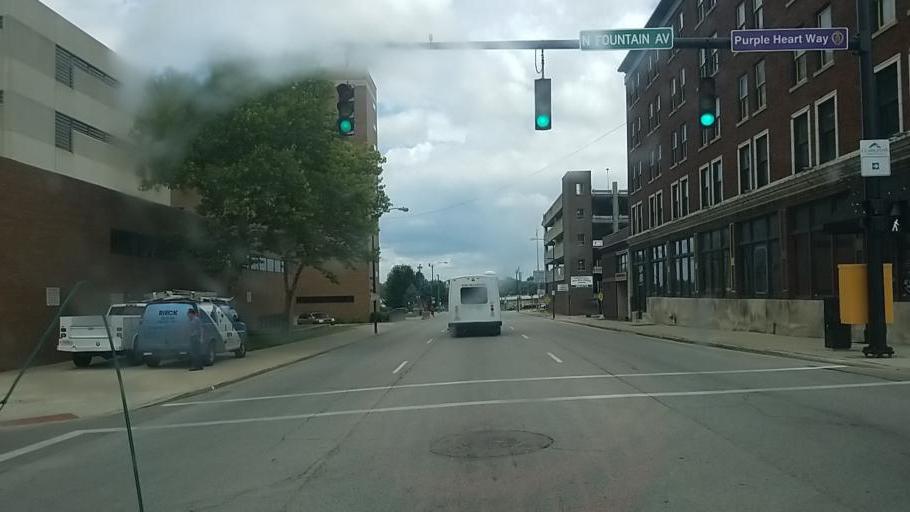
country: US
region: Ohio
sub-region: Clark County
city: Springfield
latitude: 39.9259
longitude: -83.8101
